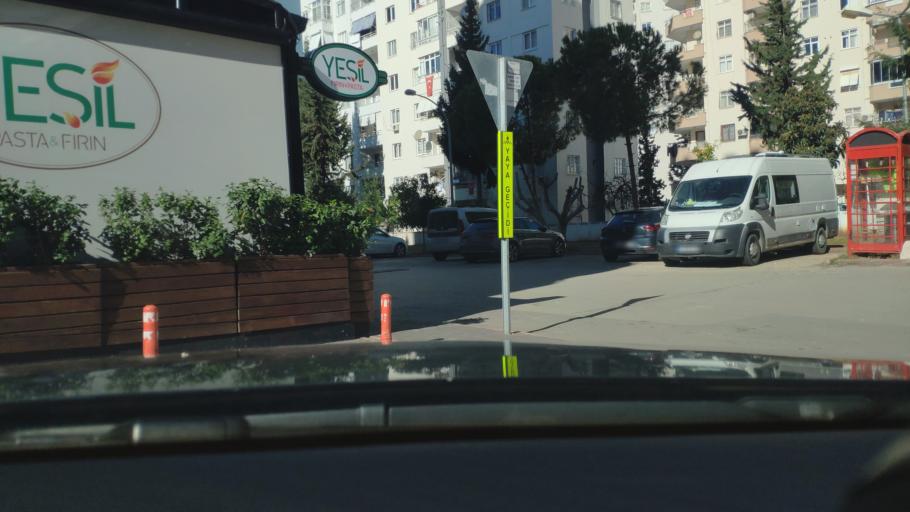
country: TR
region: Adana
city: Adana
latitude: 37.0542
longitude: 35.2814
